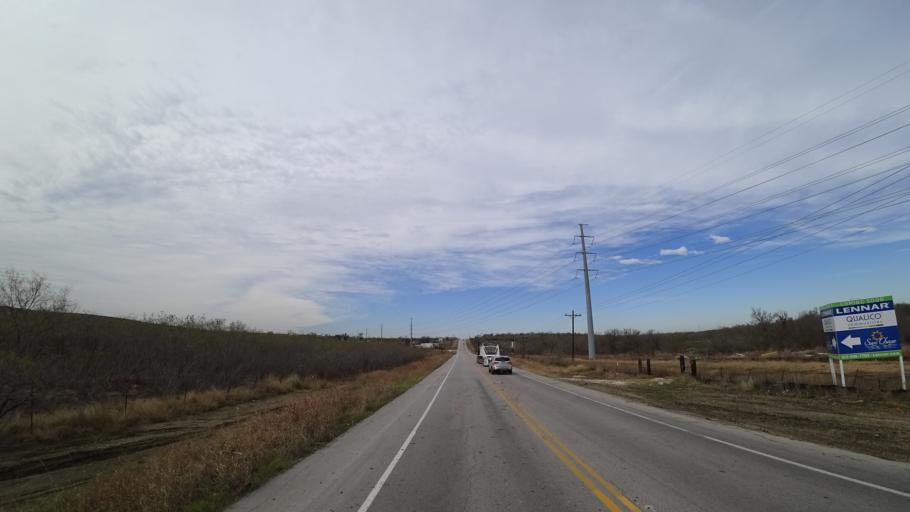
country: US
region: Texas
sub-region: Travis County
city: Garfield
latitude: 30.1534
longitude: -97.5899
